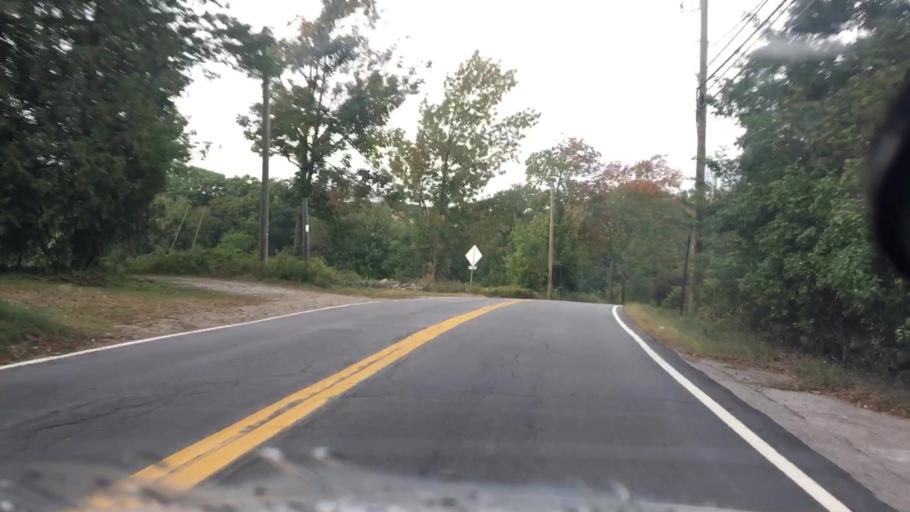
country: US
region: New Hampshire
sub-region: Carroll County
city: Sanbornville
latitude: 43.5595
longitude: -71.0295
